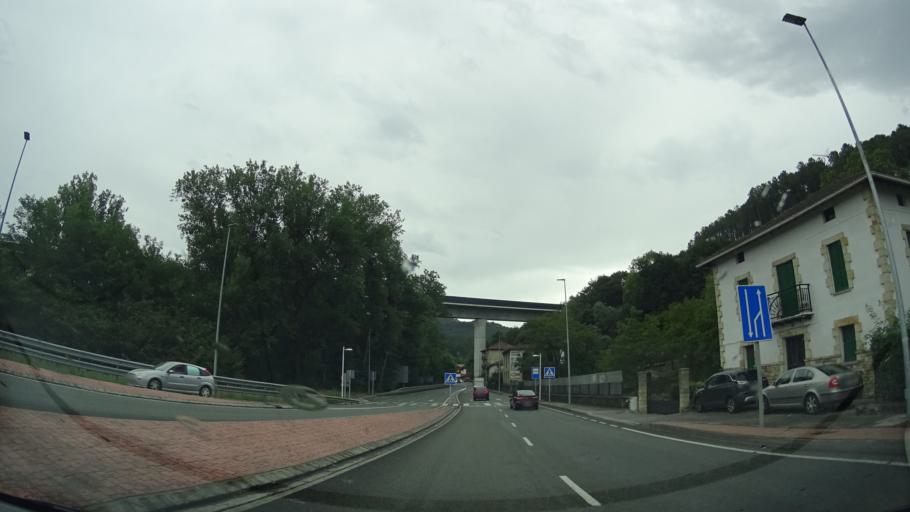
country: ES
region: Basque Country
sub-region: Bizkaia
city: Galdakao
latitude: 43.2268
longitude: -2.8196
